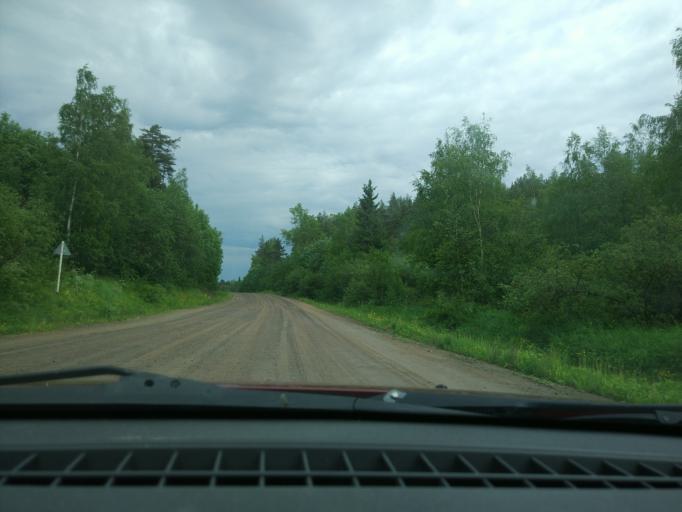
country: RU
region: Leningrad
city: Kuznechnoye
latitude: 61.2833
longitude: 29.8578
